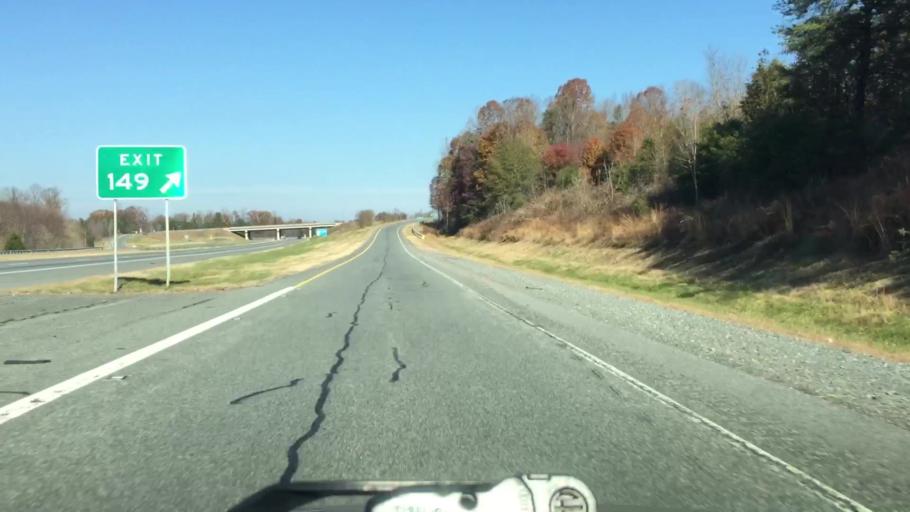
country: US
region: North Carolina
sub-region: Rockingham County
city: Reidsville
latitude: 36.3070
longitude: -79.6430
